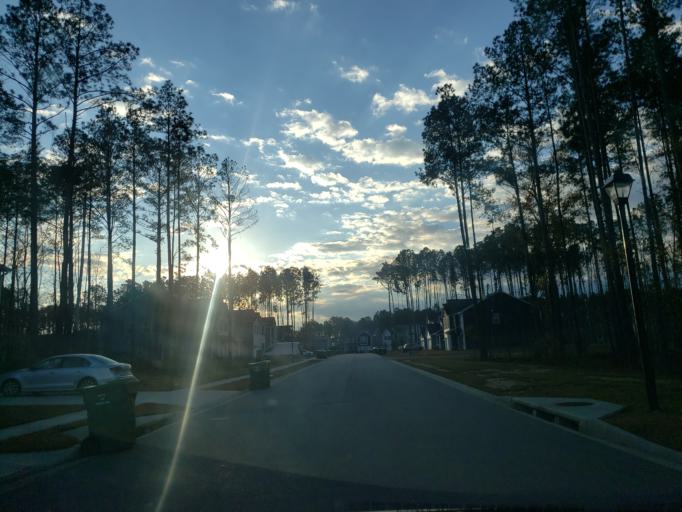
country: US
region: Georgia
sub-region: Chatham County
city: Bloomingdale
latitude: 32.1528
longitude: -81.2758
